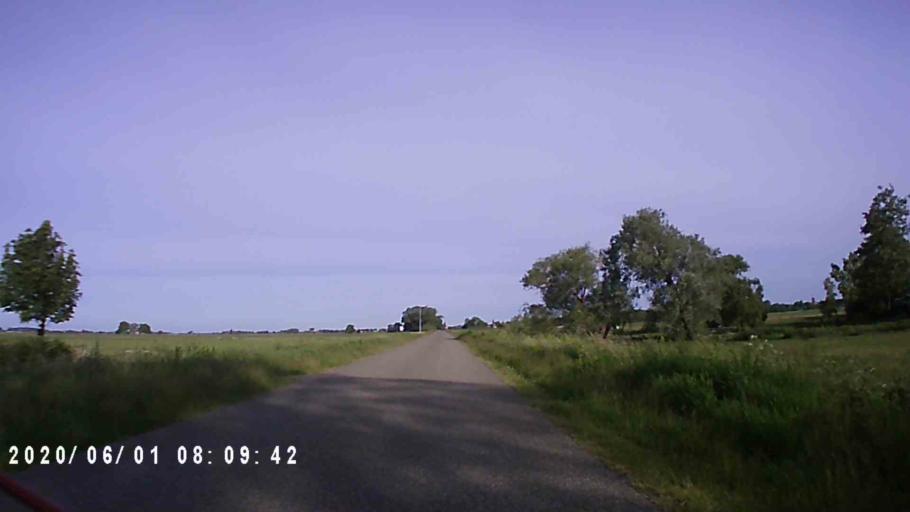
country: NL
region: Friesland
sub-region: Gemeente Ferwerderadiel
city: Burdaard
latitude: 53.2855
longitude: 5.8920
